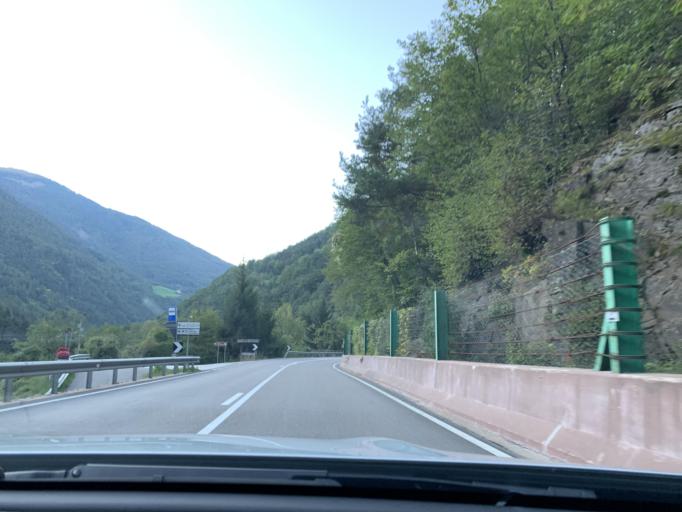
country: IT
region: Trentino-Alto Adige
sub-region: Bolzano
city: Cornedo All'Isarco
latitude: 46.4566
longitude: 11.4280
